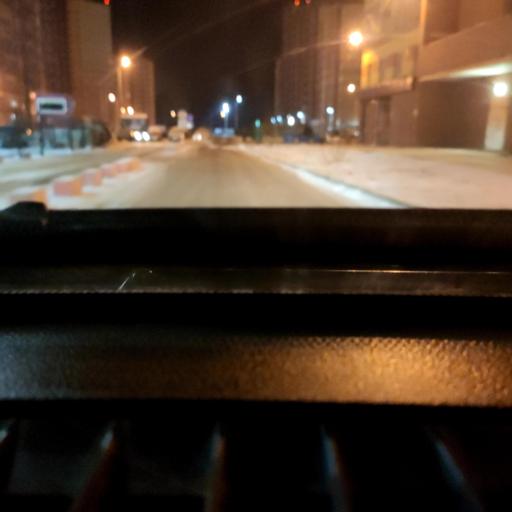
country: RU
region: Perm
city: Perm
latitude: 58.0845
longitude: 56.4043
